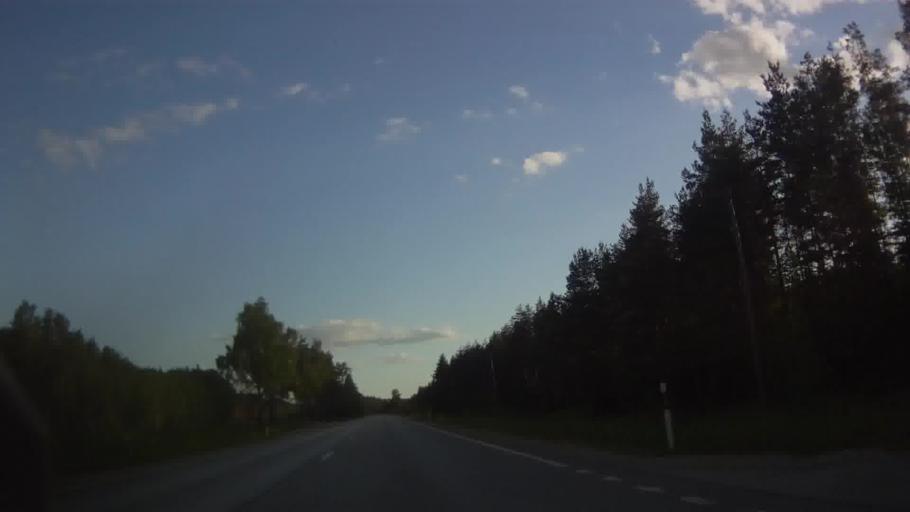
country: LV
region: Varaklani
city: Varaklani
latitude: 56.5539
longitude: 26.5985
